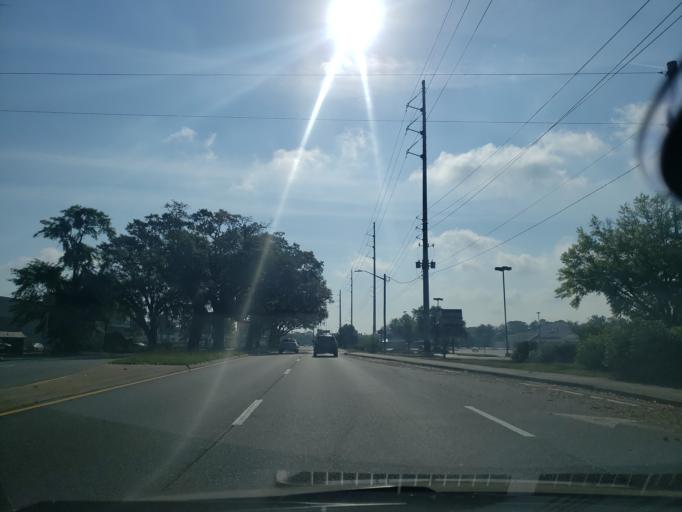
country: US
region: Georgia
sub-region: Chatham County
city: Montgomery
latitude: 31.9999
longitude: -81.1256
